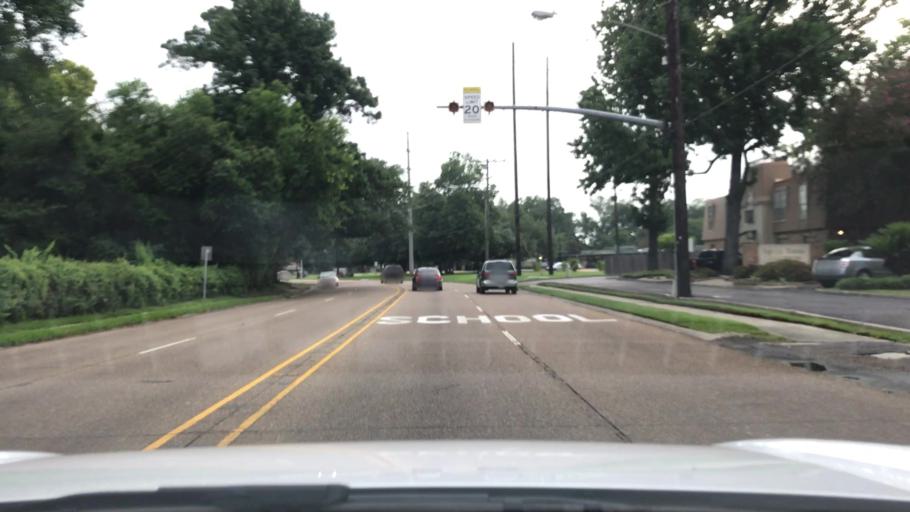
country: US
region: Louisiana
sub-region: East Baton Rouge Parish
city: Baton Rouge
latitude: 30.4291
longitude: -91.1358
